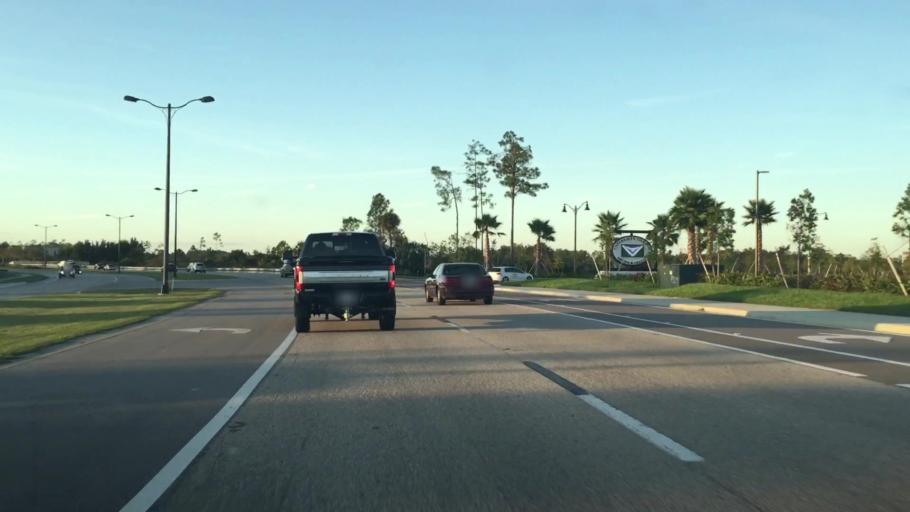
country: US
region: Florida
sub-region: Lee County
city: Three Oaks
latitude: 26.4525
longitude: -81.7747
